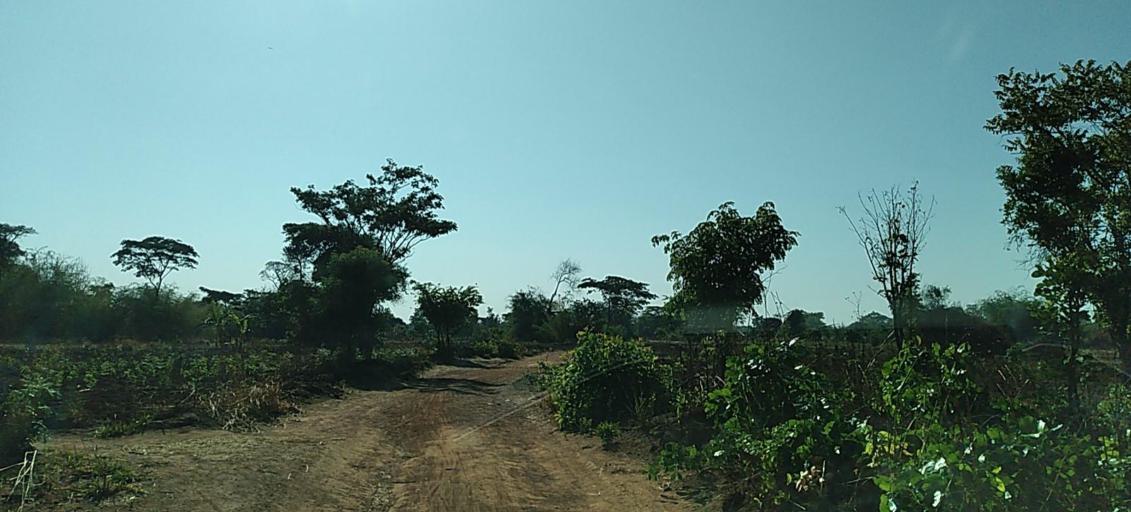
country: ZM
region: Copperbelt
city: Chililabombwe
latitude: -12.3691
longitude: 27.9111
